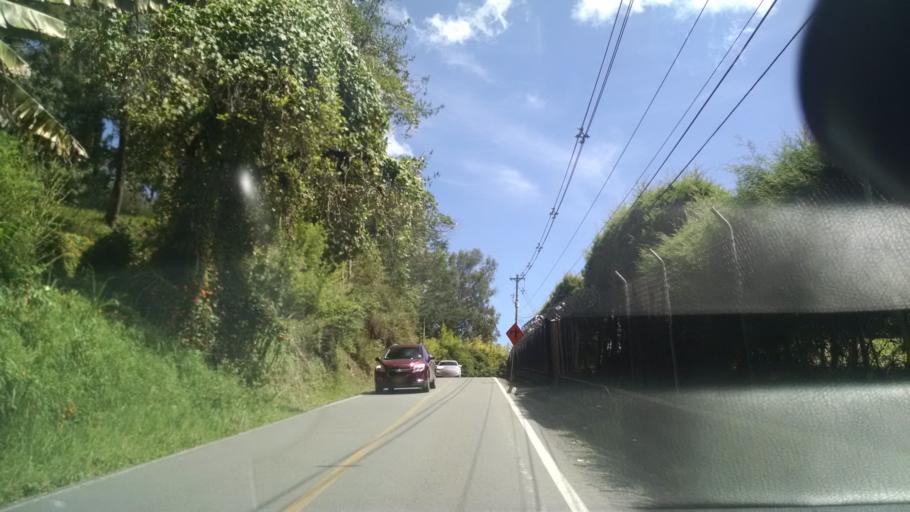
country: CO
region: Antioquia
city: El Retiro
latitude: 6.0824
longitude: -75.5011
